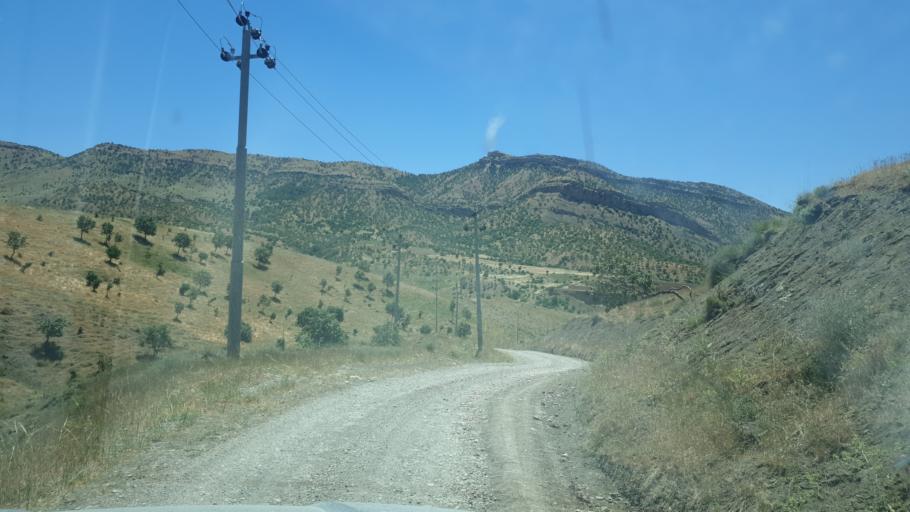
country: IQ
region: Arbil
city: Nahiyat Hiran
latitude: 36.1992
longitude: 44.4224
